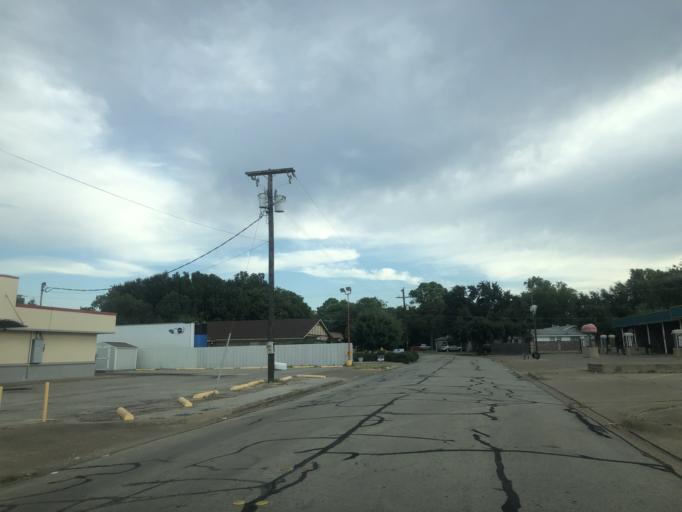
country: US
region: Texas
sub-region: Tarrant County
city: Hurst
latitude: 32.8237
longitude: -97.1598
